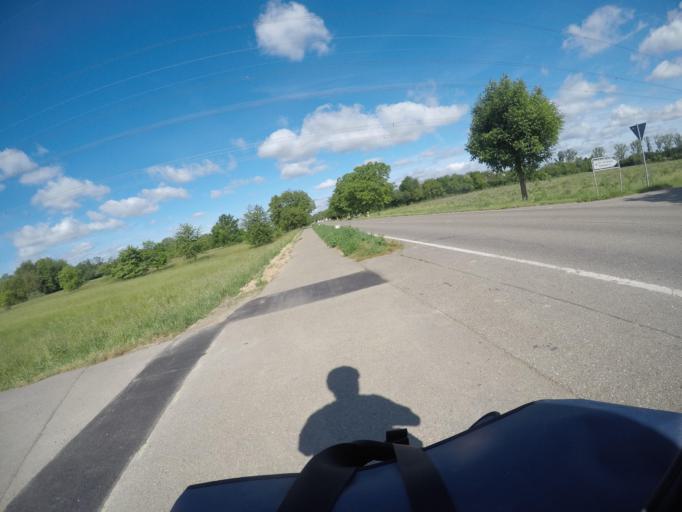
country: DE
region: Baden-Wuerttemberg
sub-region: Karlsruhe Region
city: Durmersheim
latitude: 48.9393
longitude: 8.2655
